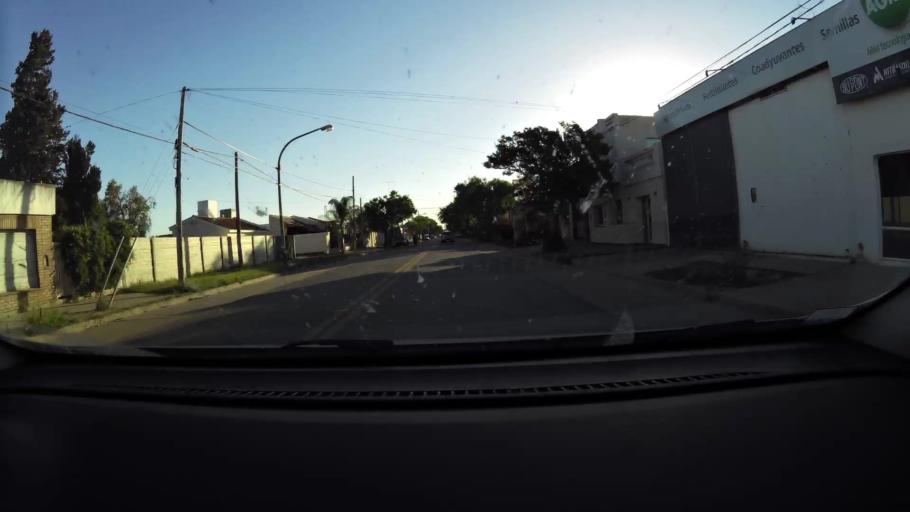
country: AR
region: Cordoba
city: Las Varillas
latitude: -31.8783
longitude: -62.7209
